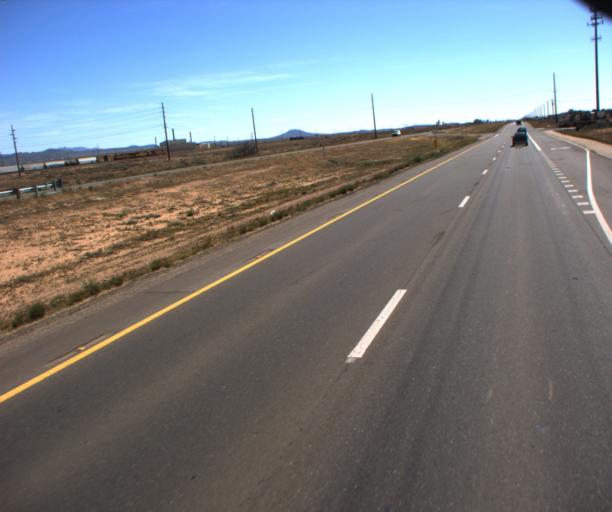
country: US
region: Arizona
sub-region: Mohave County
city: New Kingman-Butler
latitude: 35.2659
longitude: -113.9644
